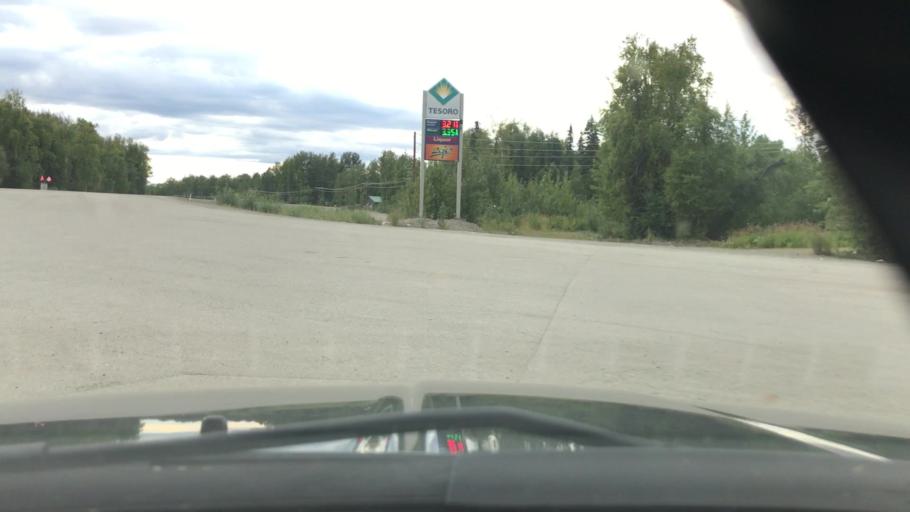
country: US
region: Alaska
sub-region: Matanuska-Susitna Borough
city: Y
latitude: 62.1368
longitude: -150.0412
